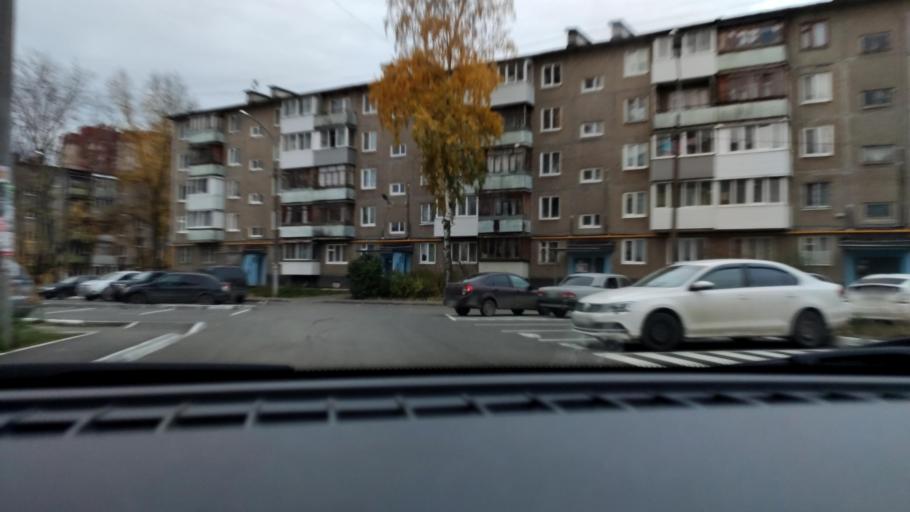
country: RU
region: Perm
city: Perm
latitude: 57.9616
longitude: 56.2234
